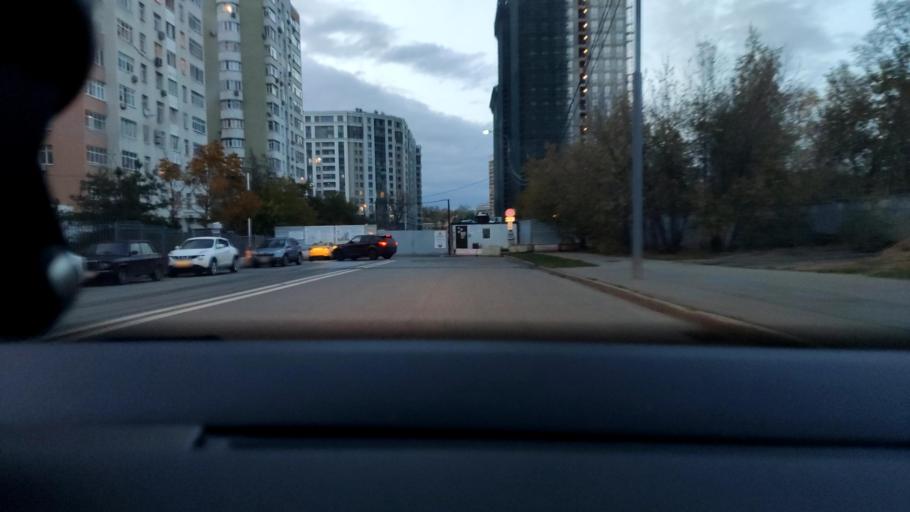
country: RU
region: Moscow
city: Sokol
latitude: 55.7929
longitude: 37.5288
